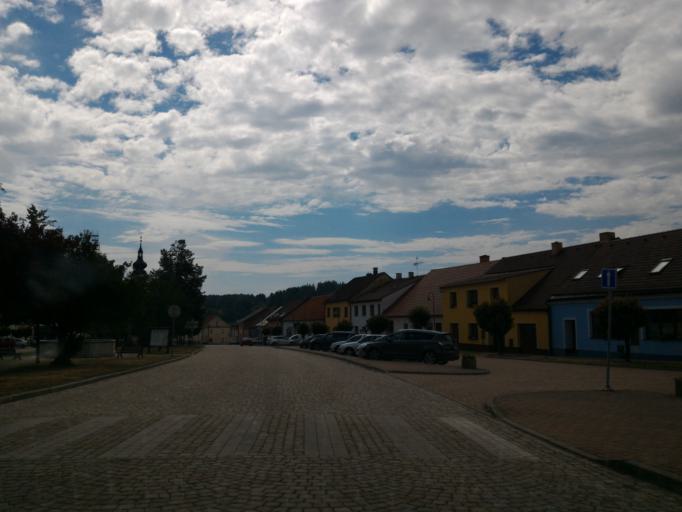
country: CZ
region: Vysocina
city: Zeletava
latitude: 49.1402
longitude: 15.5614
